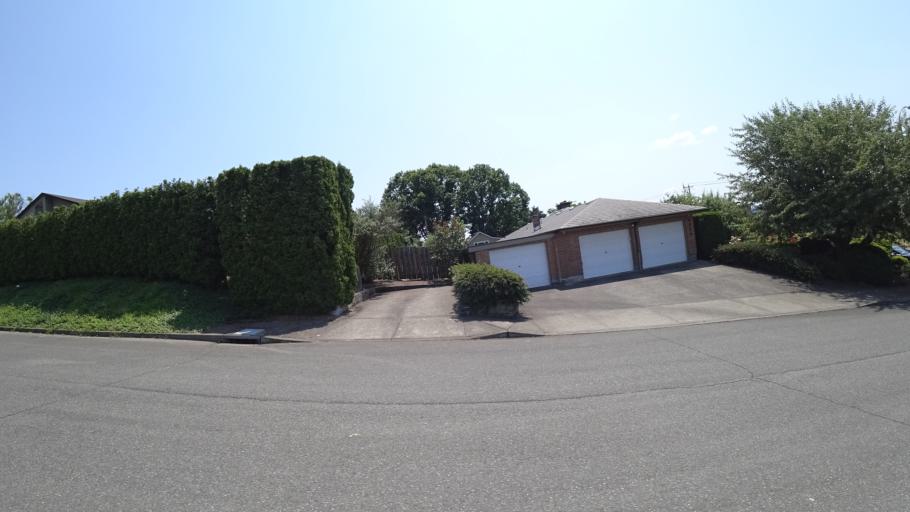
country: US
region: Oregon
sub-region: Multnomah County
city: Lents
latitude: 45.4514
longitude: -122.5683
